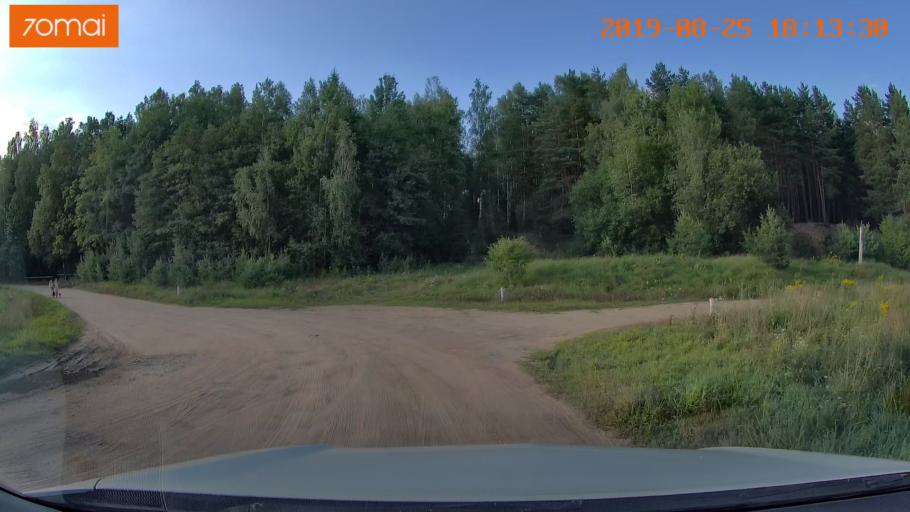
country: BY
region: Minsk
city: Khatsyezhyna
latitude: 53.9441
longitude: 27.3067
